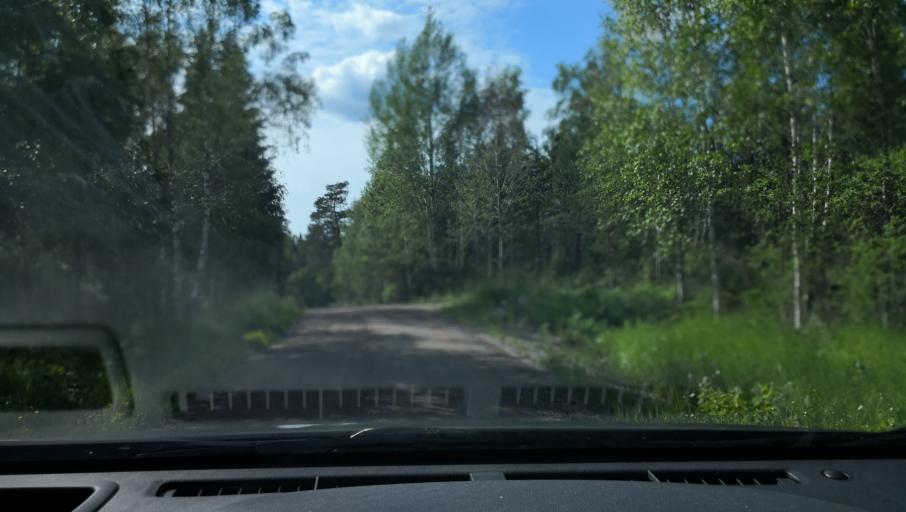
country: SE
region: Uppsala
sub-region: Enkopings Kommun
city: Orsundsbro
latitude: 59.8346
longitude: 17.2342
